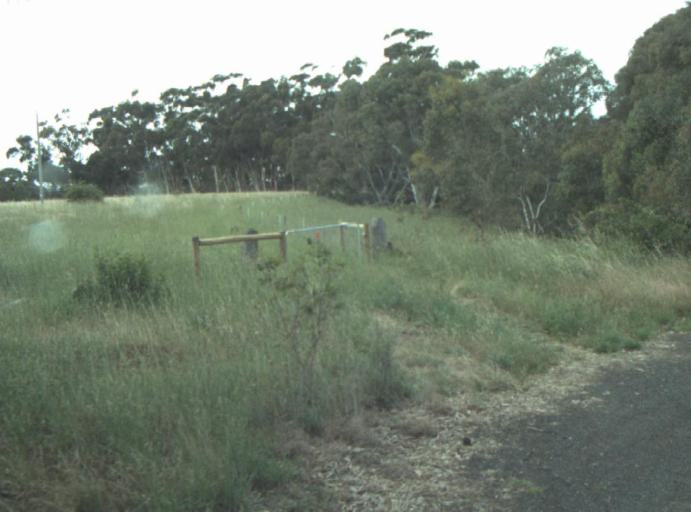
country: AU
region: Victoria
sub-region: Wyndham
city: Wyndham Vale
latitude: -37.8433
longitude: 144.3549
